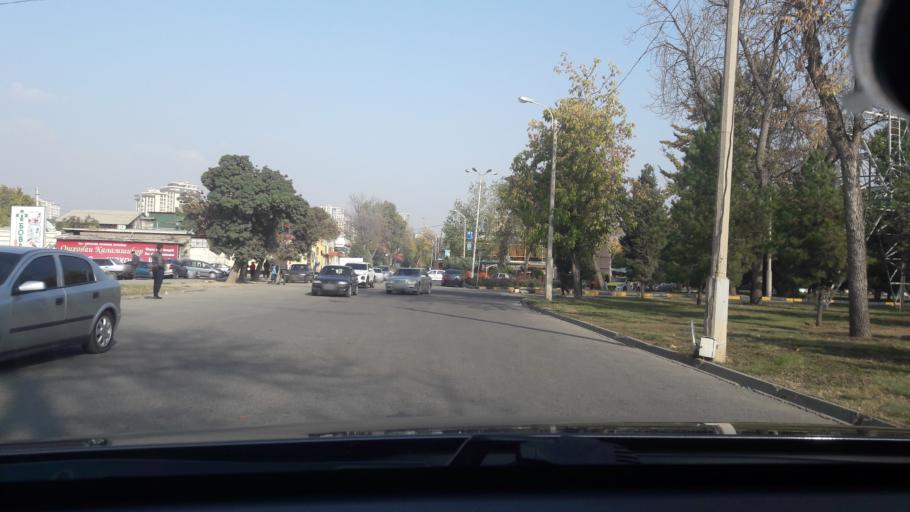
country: TJ
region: Dushanbe
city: Dushanbe
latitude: 38.5615
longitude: 68.7749
